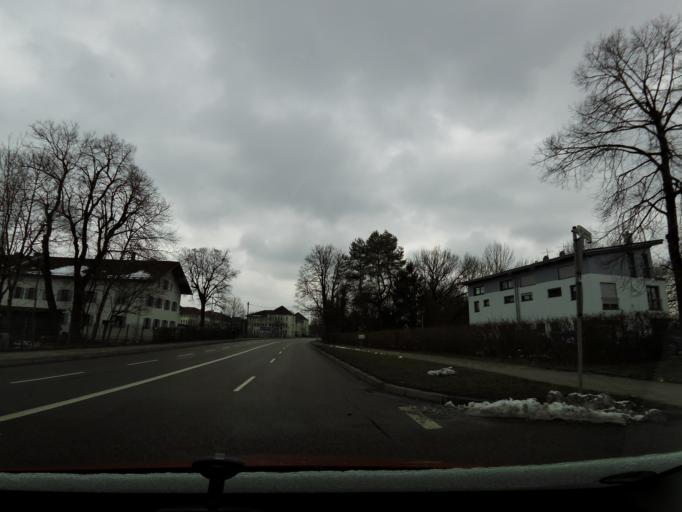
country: DE
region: Bavaria
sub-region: Upper Bavaria
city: Unterfoehring
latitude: 48.1858
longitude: 11.6340
